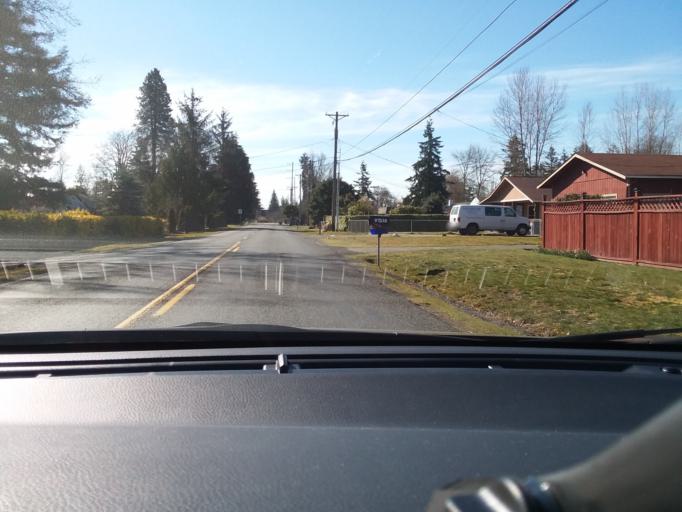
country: US
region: Washington
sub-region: Pierce County
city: Midland
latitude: 47.1719
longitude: -122.3972
